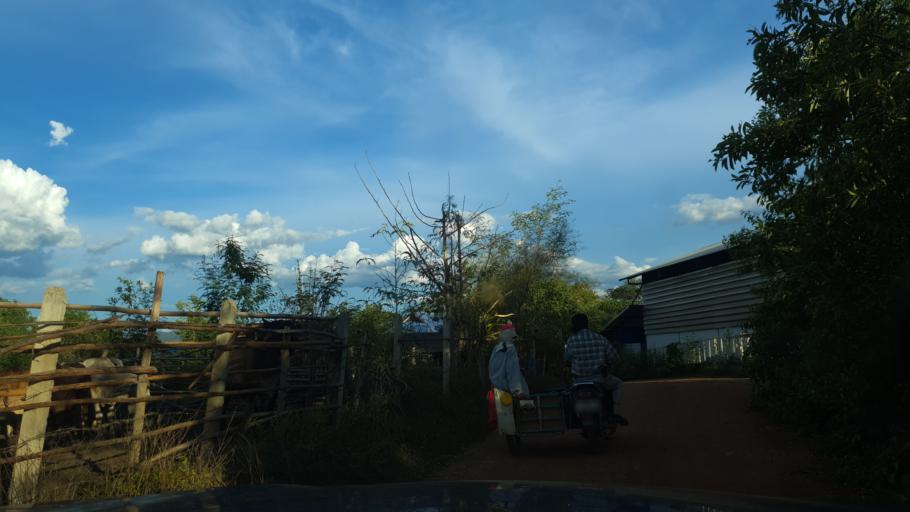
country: TH
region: Lampang
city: Sop Prap
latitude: 17.9527
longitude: 99.3492
